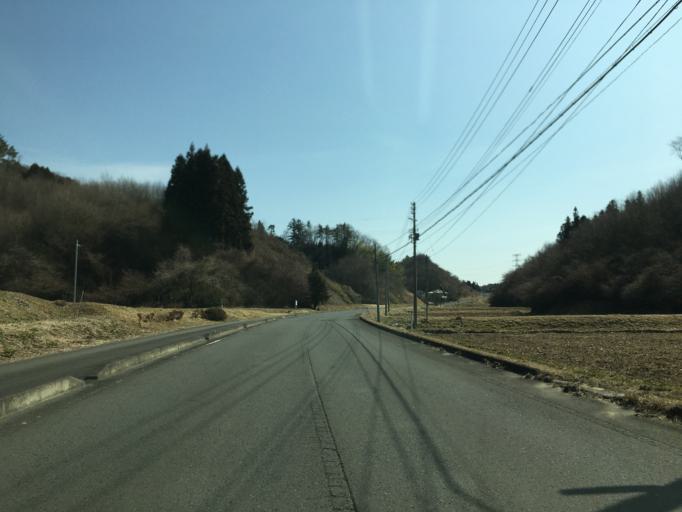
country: JP
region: Fukushima
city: Ishikawa
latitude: 37.0438
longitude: 140.4693
